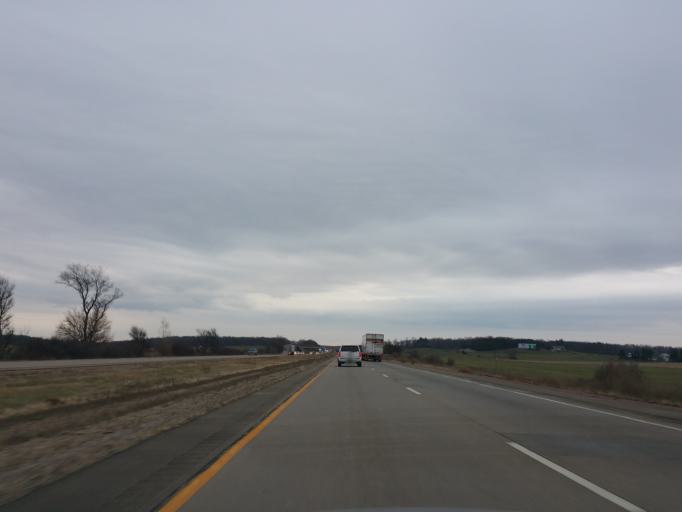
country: US
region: Wisconsin
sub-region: Sauk County
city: Lake Delton
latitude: 43.5613
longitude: -89.7273
